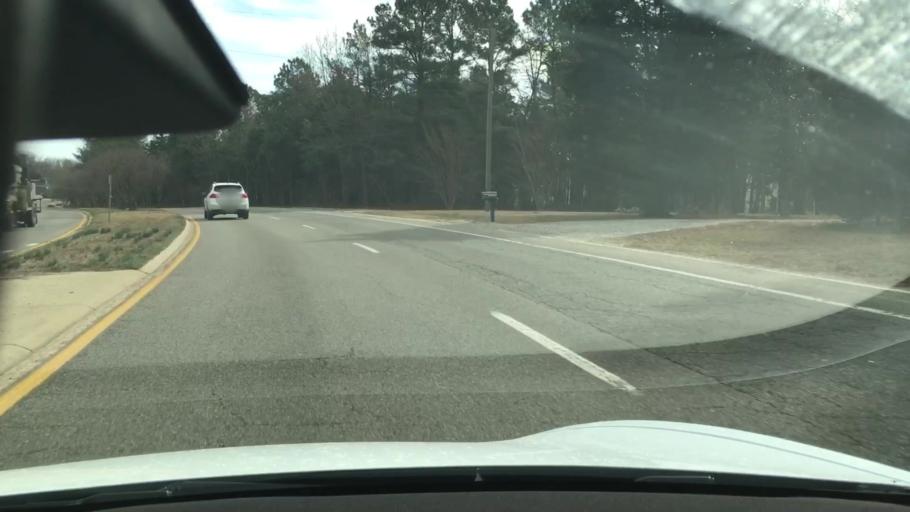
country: US
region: Virginia
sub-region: Chesterfield County
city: Bon Air
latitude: 37.5287
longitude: -77.6276
